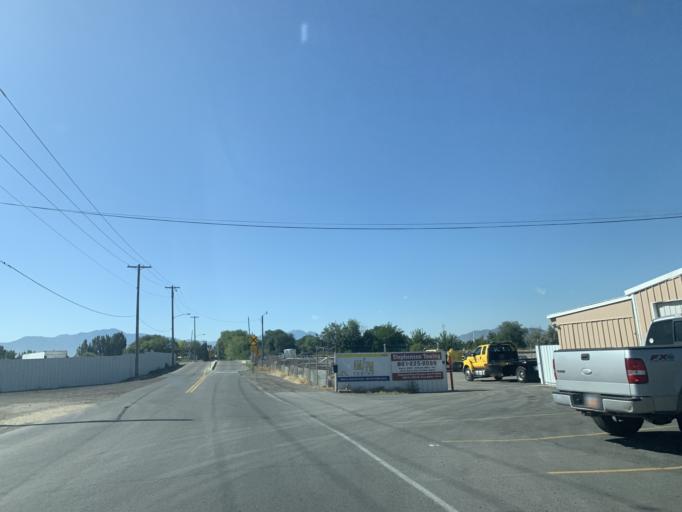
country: US
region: Utah
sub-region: Utah County
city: Orem
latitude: 40.2606
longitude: -111.7083
